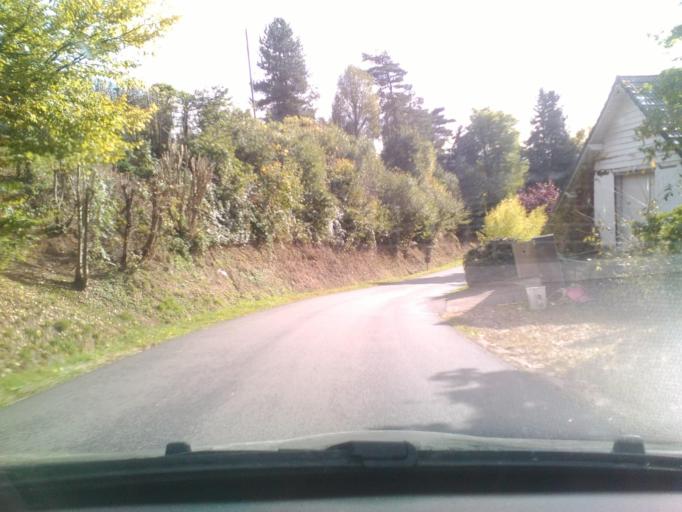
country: FR
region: Lorraine
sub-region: Departement des Vosges
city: Sainte-Marguerite
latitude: 48.2787
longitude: 6.9844
